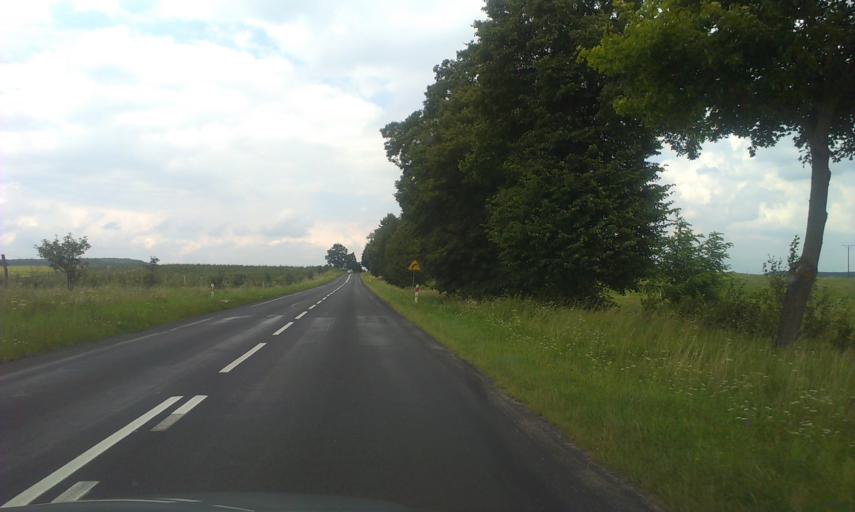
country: PL
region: West Pomeranian Voivodeship
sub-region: Powiat swidwinski
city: Polczyn-Zdroj
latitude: 53.8779
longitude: 16.0688
